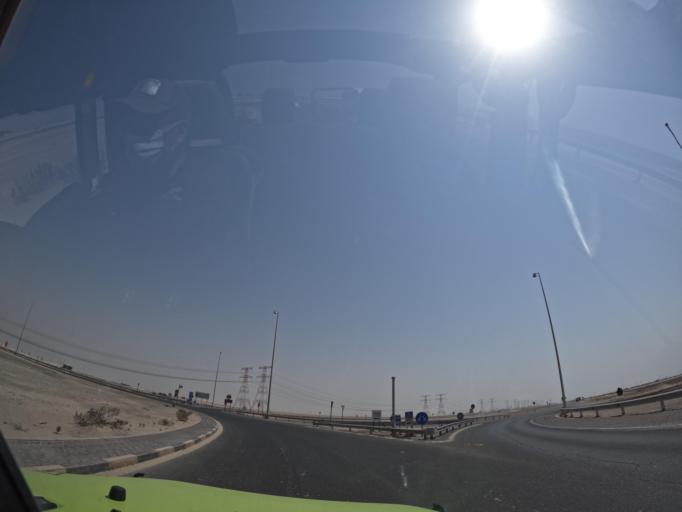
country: AE
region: Abu Dhabi
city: Abu Dhabi
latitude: 24.2026
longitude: 54.4199
